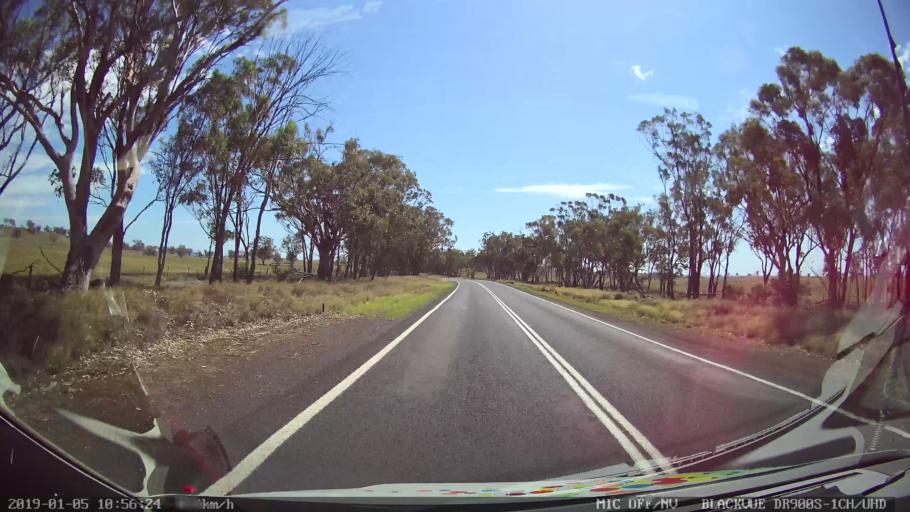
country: AU
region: New South Wales
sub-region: Warrumbungle Shire
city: Coonabarabran
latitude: -31.4416
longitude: 149.1576
